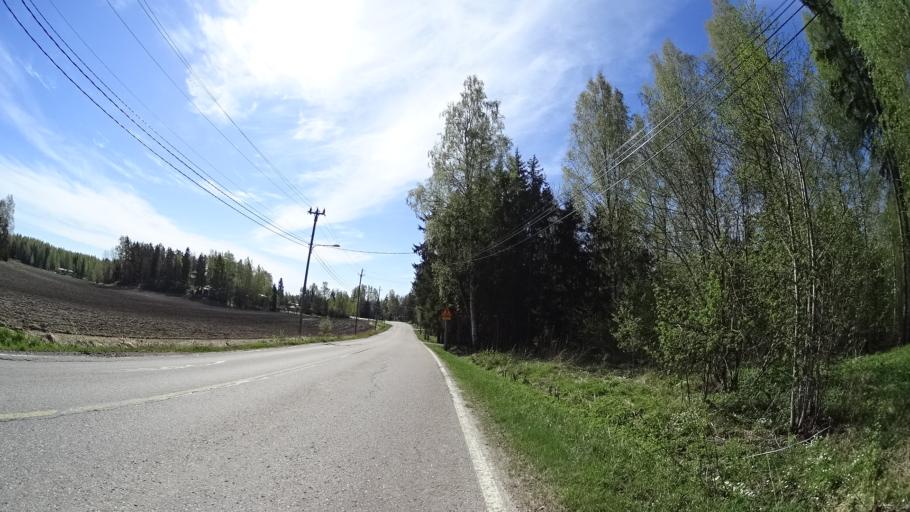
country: FI
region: Uusimaa
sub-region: Helsinki
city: Nurmijaervi
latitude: 60.3710
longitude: 24.8378
